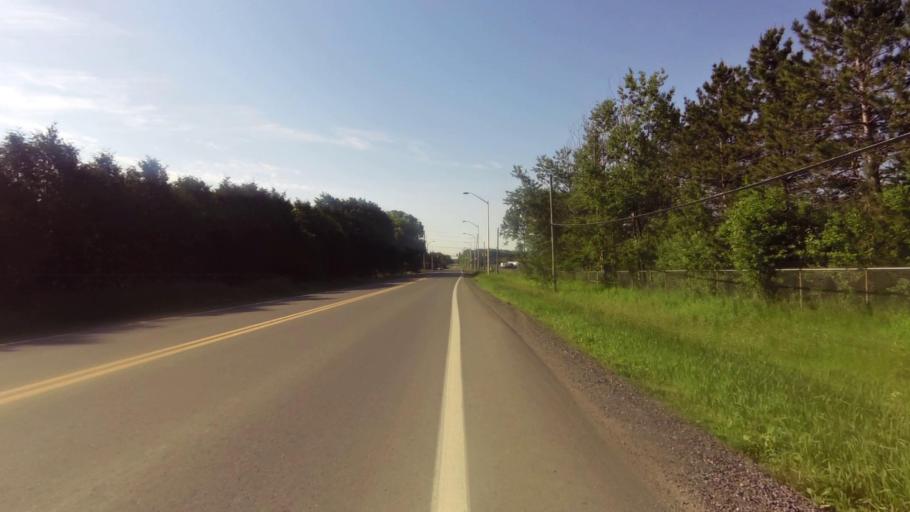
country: CA
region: Ontario
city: Ottawa
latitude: 45.2609
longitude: -75.5697
